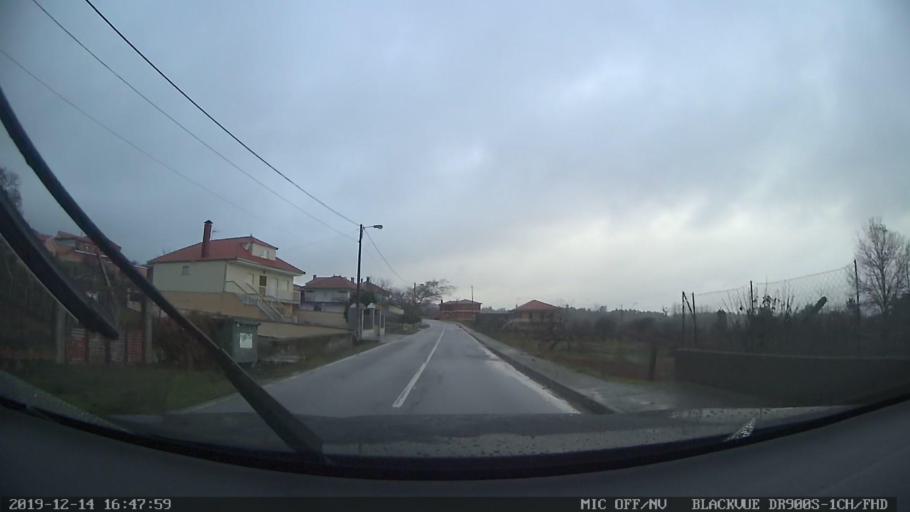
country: PT
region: Vila Real
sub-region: Murca
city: Murca
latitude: 41.4028
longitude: -7.5000
